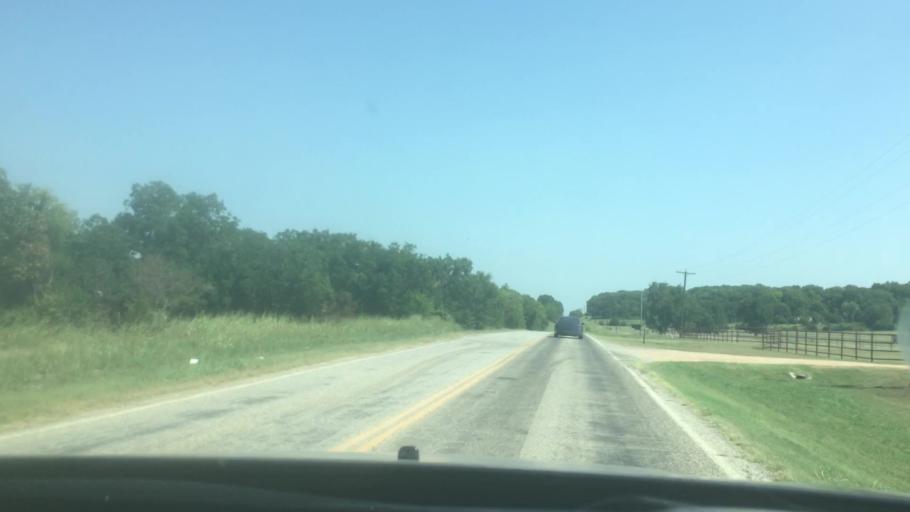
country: US
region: Oklahoma
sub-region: Coal County
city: Coalgate
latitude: 34.3592
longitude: -96.4245
